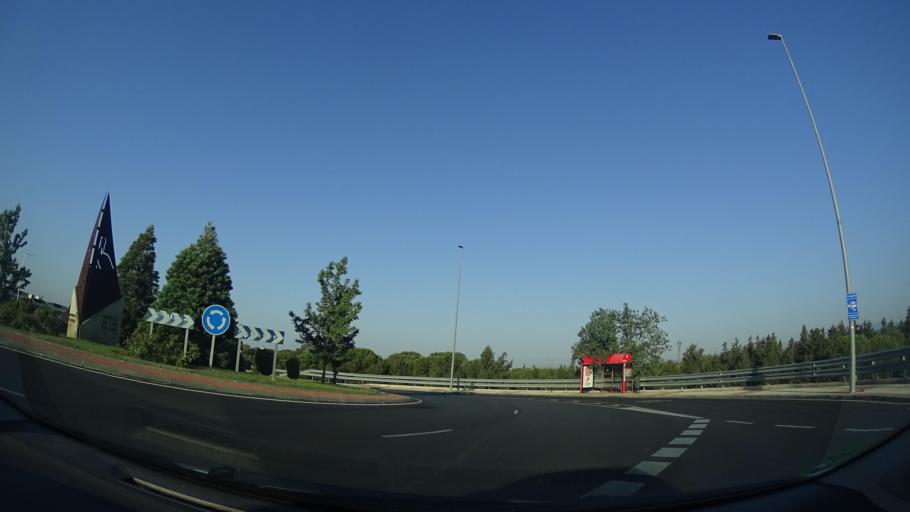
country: ES
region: Madrid
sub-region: Provincia de Madrid
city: Las Rozas de Madrid
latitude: 40.5086
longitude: -3.8799
